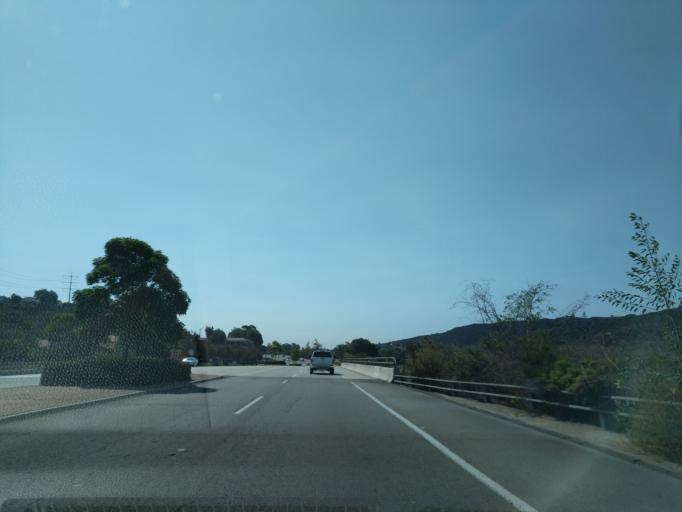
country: US
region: California
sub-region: San Diego County
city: Encinitas
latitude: 33.0886
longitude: -117.2694
